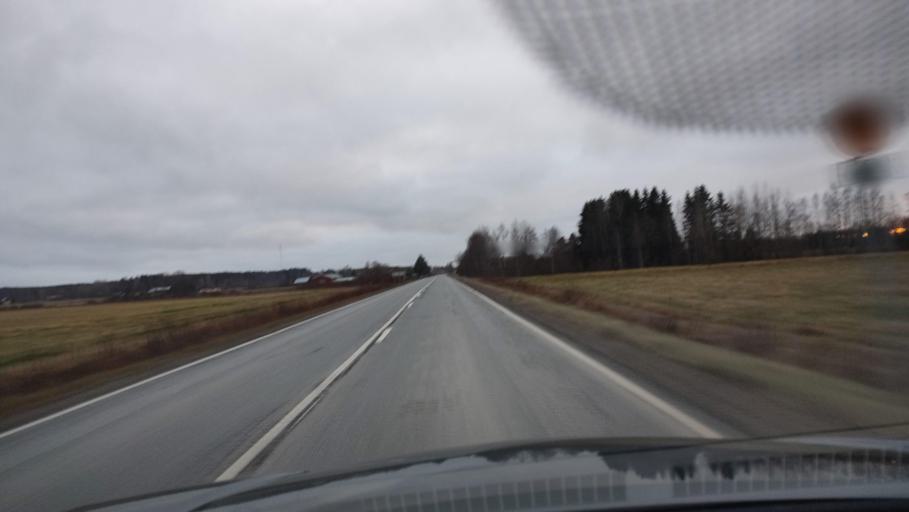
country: FI
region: Southern Ostrobothnia
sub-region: Suupohja
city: Kauhajoki
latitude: 62.3687
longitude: 22.0763
